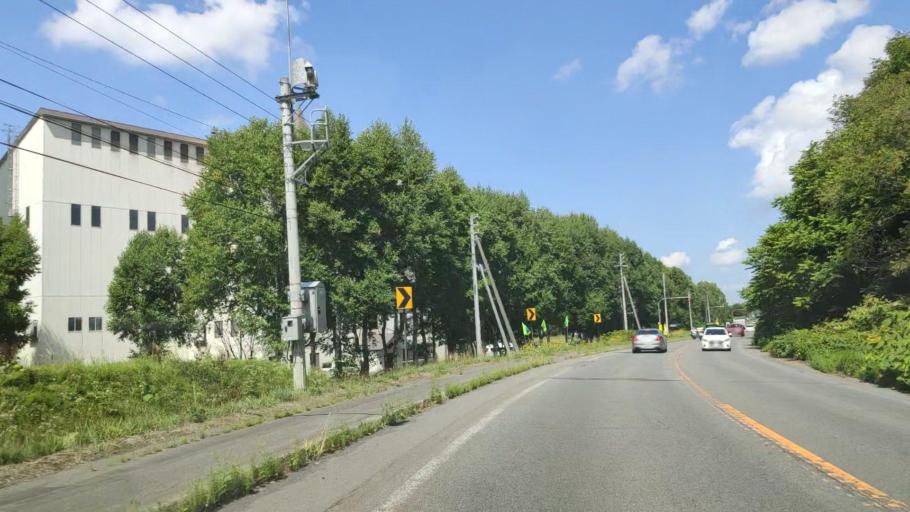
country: JP
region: Hokkaido
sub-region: Asahikawa-shi
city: Asahikawa
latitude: 43.6210
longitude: 142.4696
